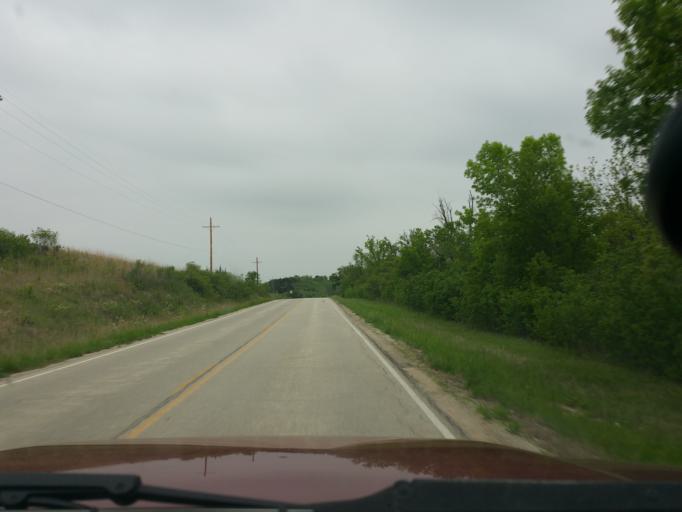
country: US
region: Kansas
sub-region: Riley County
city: Manhattan
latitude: 39.2602
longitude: -96.5697
